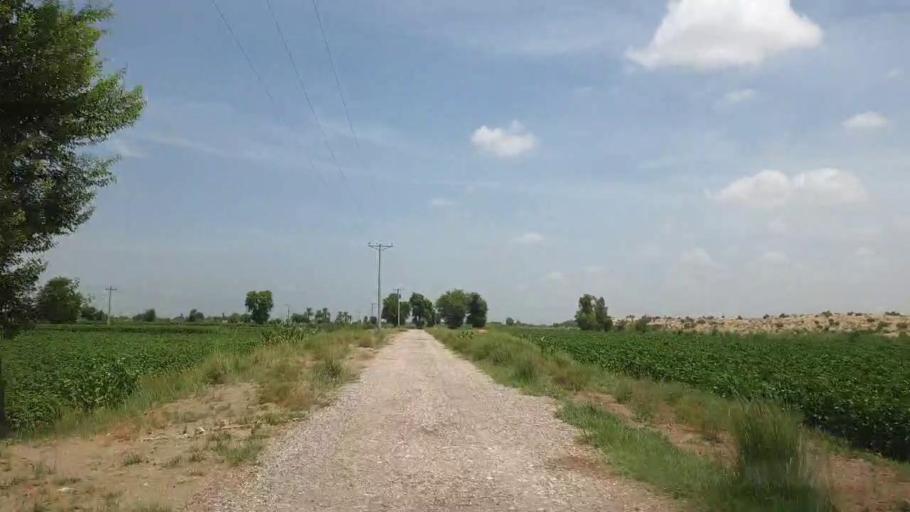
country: PK
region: Sindh
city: Kot Diji
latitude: 27.1500
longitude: 69.0170
